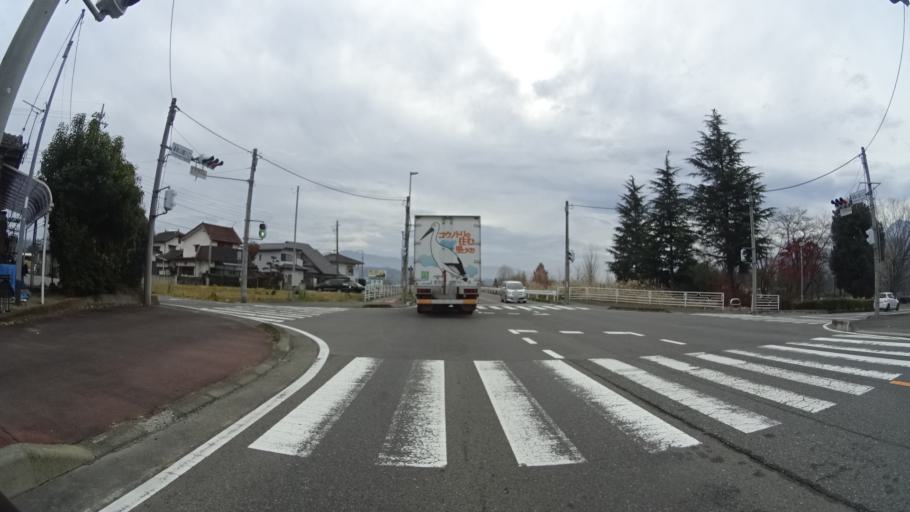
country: JP
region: Gunma
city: Numata
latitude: 36.6500
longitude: 139.0244
